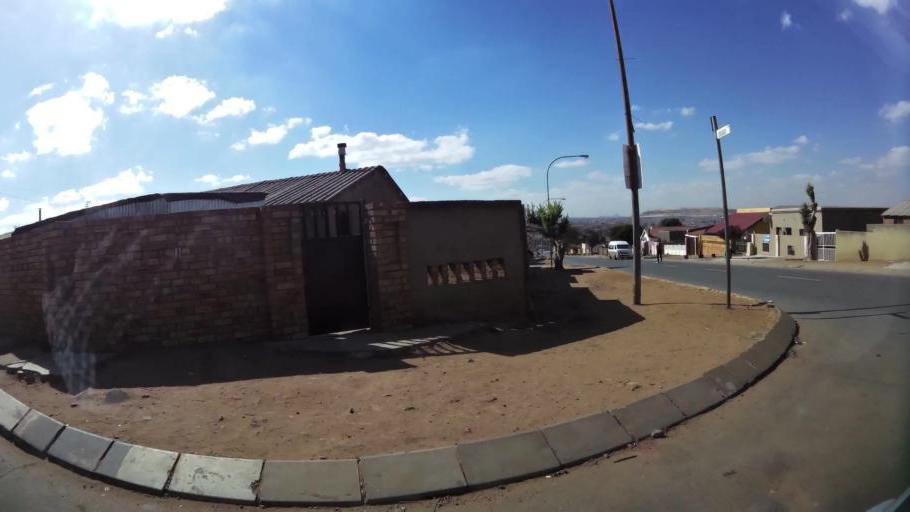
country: ZA
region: Gauteng
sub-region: City of Johannesburg Metropolitan Municipality
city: Soweto
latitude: -26.2288
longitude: 27.9017
